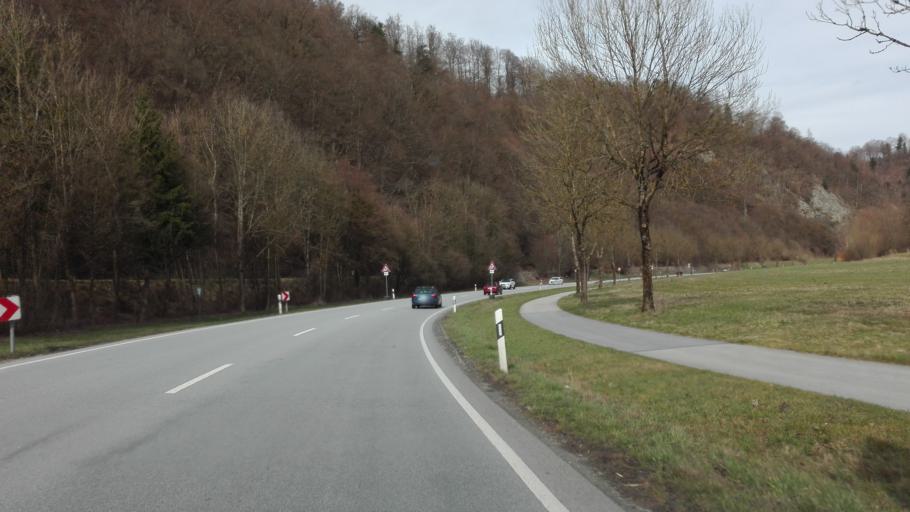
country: DE
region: Bavaria
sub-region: Lower Bavaria
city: Witzmannsberg
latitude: 48.5903
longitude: 13.5050
